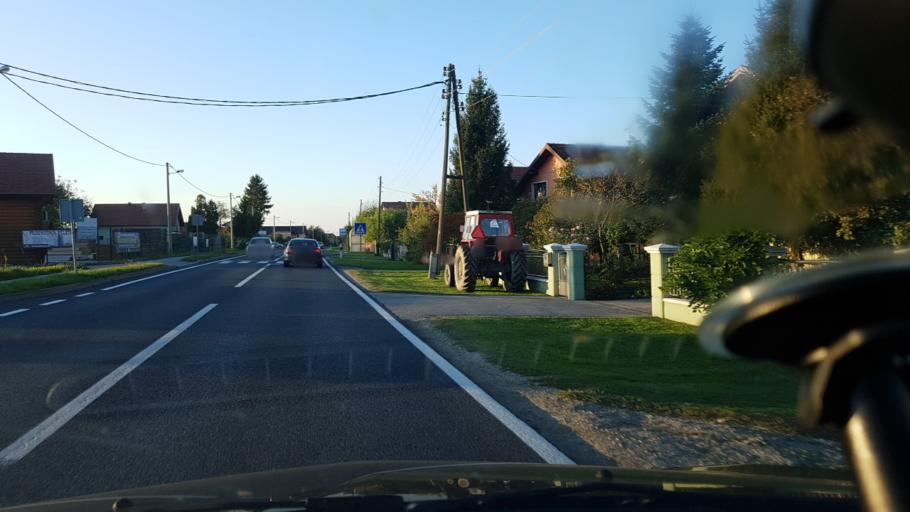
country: HR
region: Koprivnicko-Krizevacka
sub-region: Grad Koprivnica
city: Koprivnica
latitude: 46.1253
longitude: 16.8719
